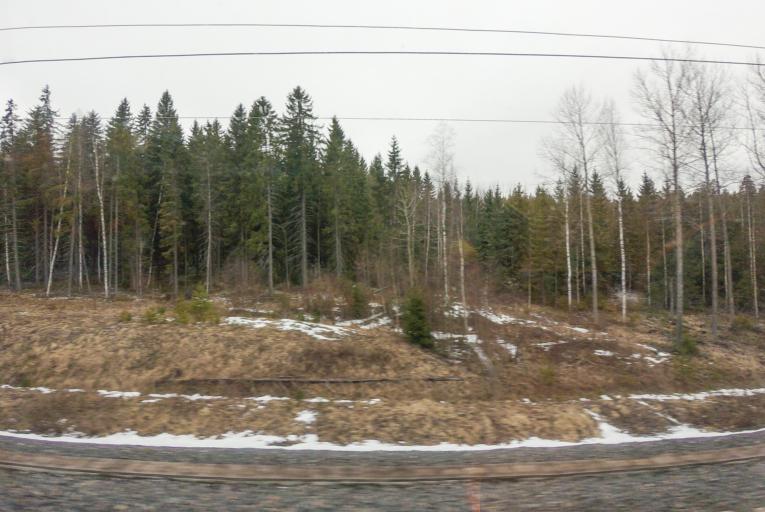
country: FI
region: Uusimaa
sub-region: Helsinki
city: Maentsaelae
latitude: 60.6018
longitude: 25.2480
